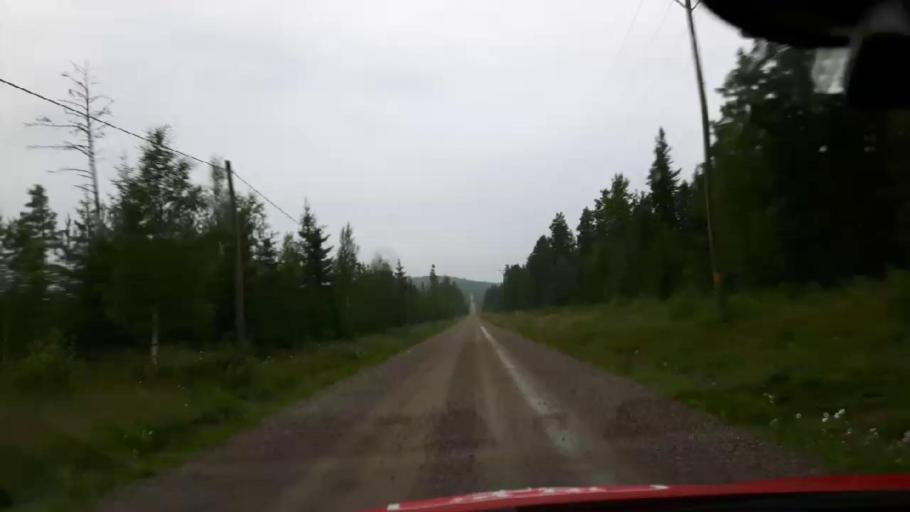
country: SE
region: Jaemtland
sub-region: OEstersunds Kommun
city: Brunflo
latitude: 62.7742
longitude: 14.9914
